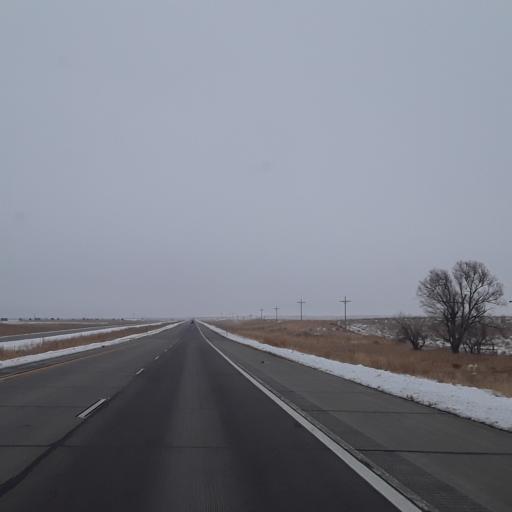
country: US
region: Colorado
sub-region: Logan County
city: Sterling
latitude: 40.5237
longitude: -103.2386
